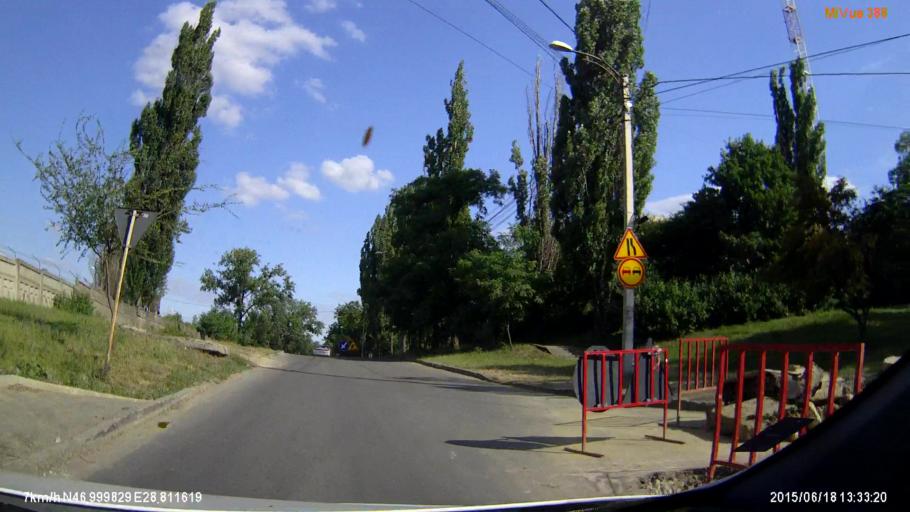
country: MD
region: Chisinau
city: Chisinau
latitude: 46.9998
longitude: 28.8115
